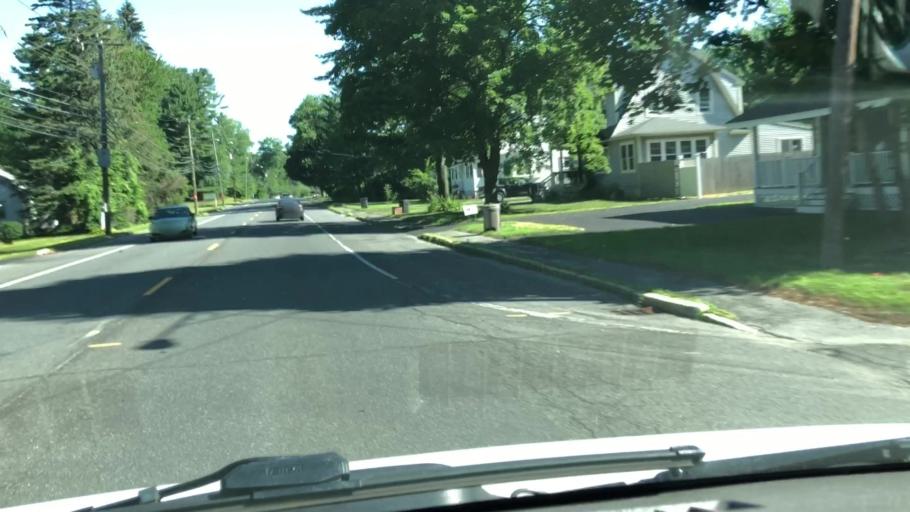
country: US
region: Massachusetts
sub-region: Berkshire County
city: Dalton
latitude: 42.4753
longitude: -73.2046
